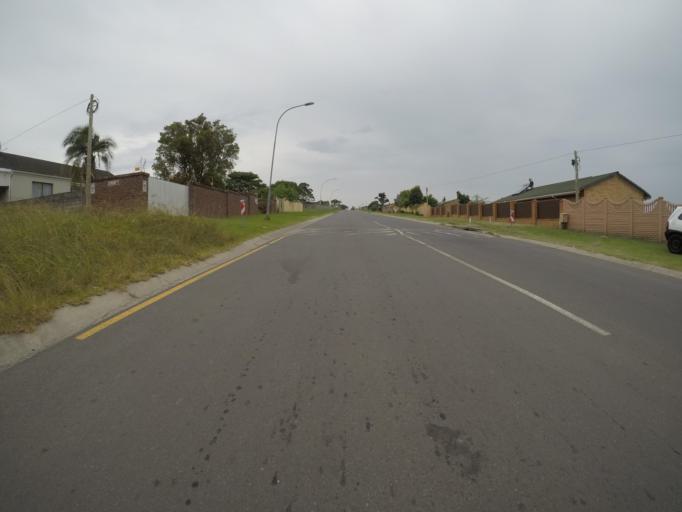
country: ZA
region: Eastern Cape
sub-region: Buffalo City Metropolitan Municipality
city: East London
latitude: -33.0012
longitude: 27.8582
